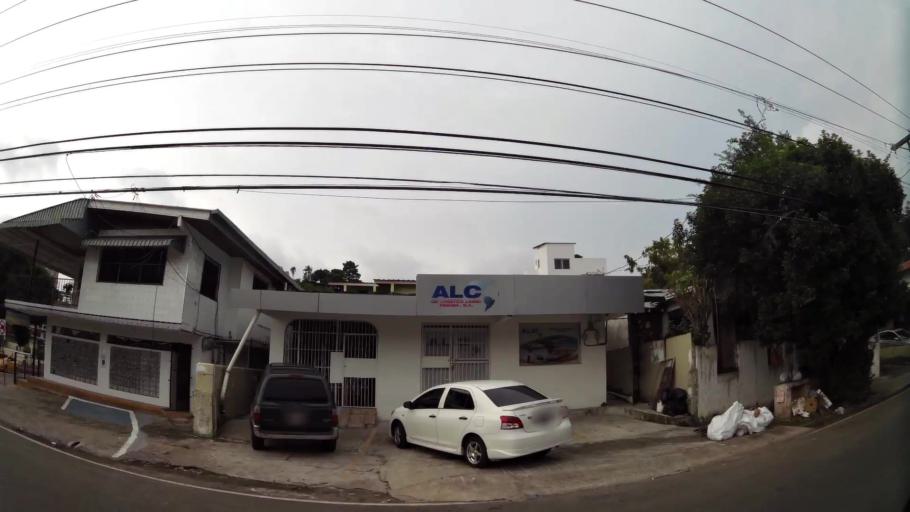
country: PA
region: Panama
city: Panama
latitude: 9.0103
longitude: -79.5279
